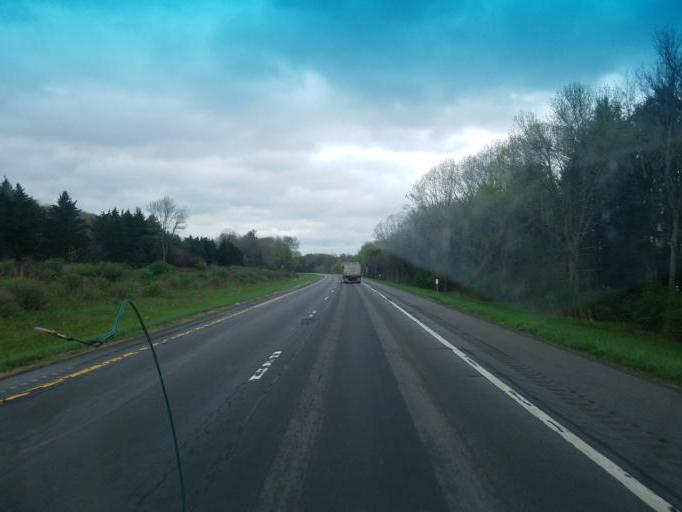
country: US
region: New York
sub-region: Chautauqua County
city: Falconer
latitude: 42.1344
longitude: -79.1449
